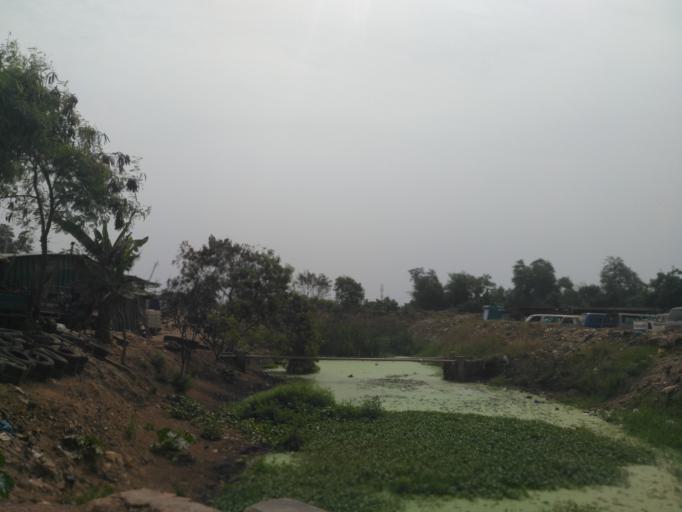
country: GH
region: Greater Accra
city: Nungua
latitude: 5.5921
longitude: -0.0917
